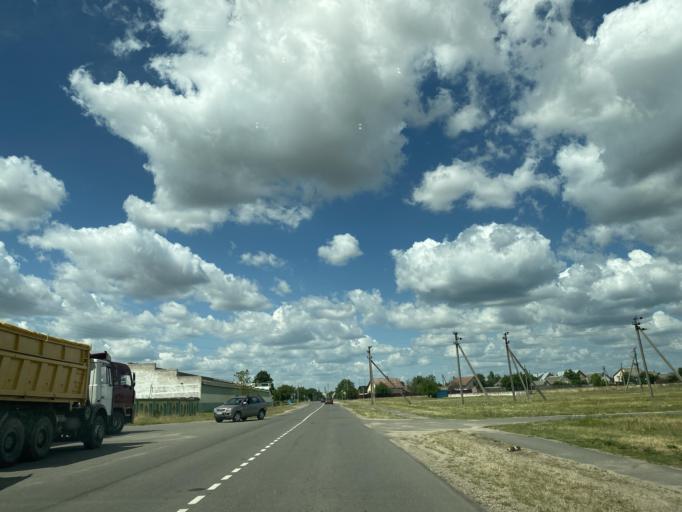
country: BY
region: Brest
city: Ivanava
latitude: 52.1404
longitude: 25.5506
